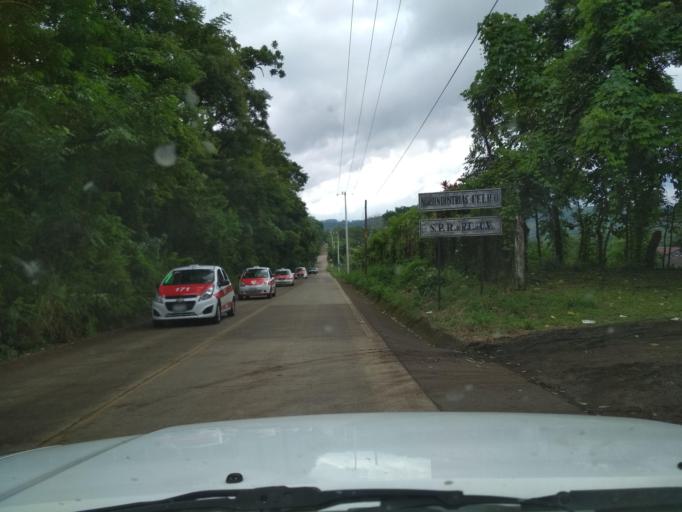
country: MX
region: Veracruz
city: Comoapan
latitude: 18.4196
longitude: -95.1772
